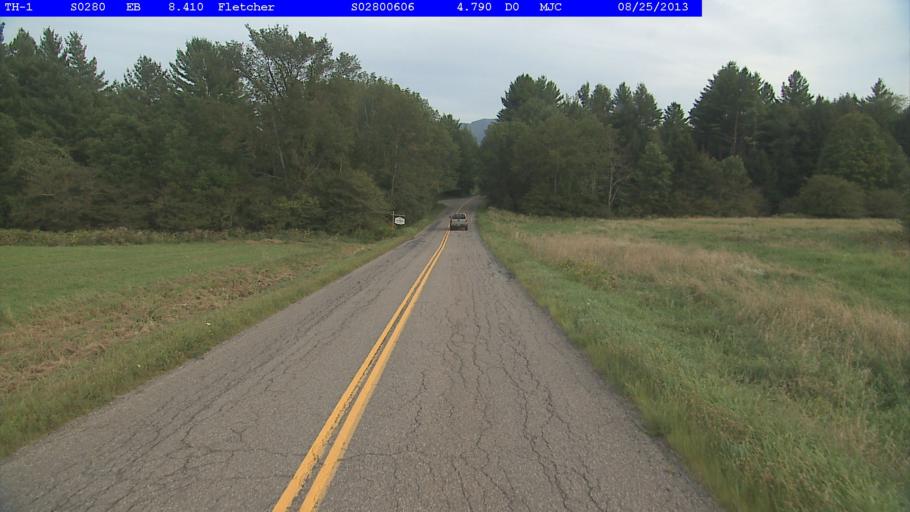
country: US
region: Vermont
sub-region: Chittenden County
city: Jericho
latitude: 44.6634
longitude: -72.8884
